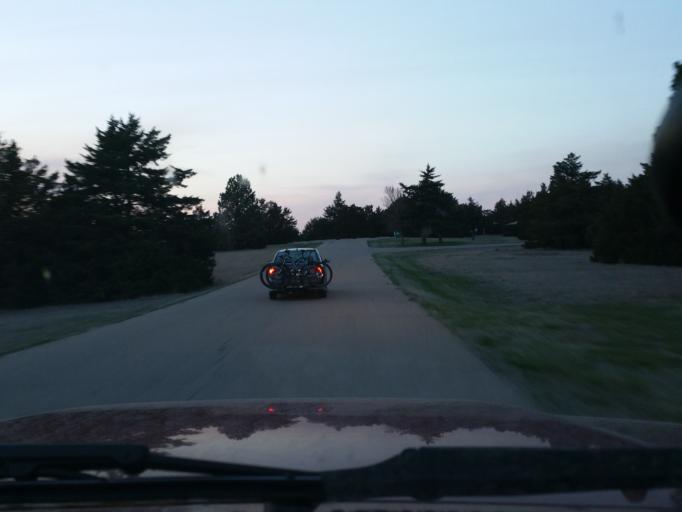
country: US
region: Kansas
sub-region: Marshall County
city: Blue Rapids
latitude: 39.4426
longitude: -96.7358
